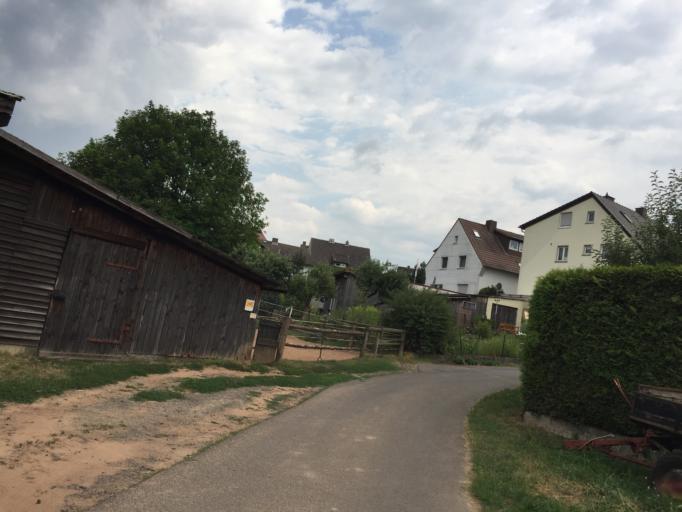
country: DE
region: Hesse
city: Staufenberg
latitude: 50.6623
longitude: 8.7236
